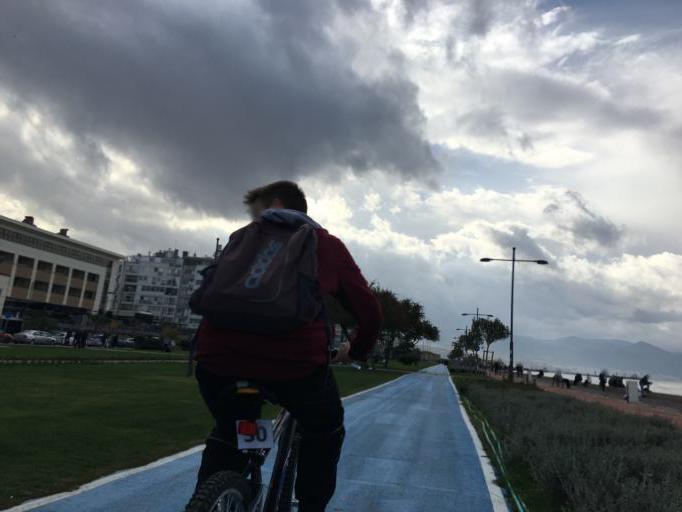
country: TR
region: Izmir
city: Izmir
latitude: 38.4338
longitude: 27.1376
